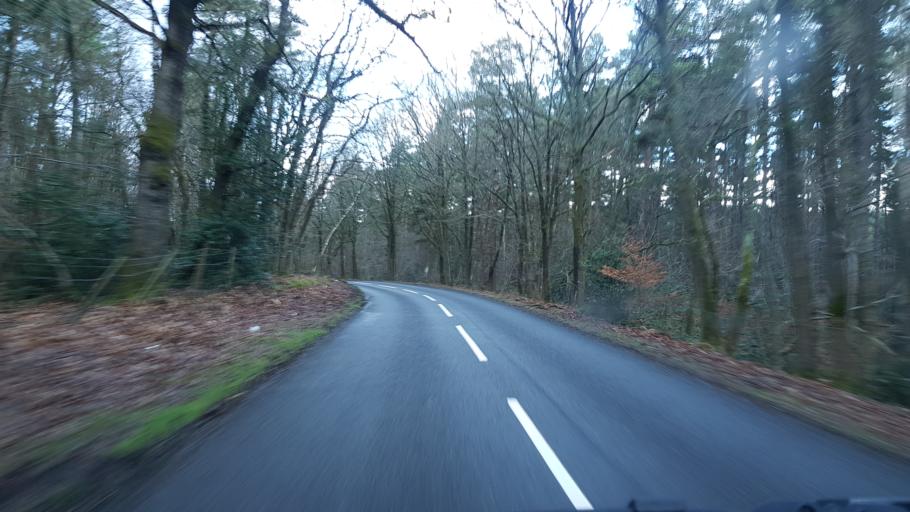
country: GB
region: England
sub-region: Surrey
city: Elstead
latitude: 51.1971
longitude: -0.7169
